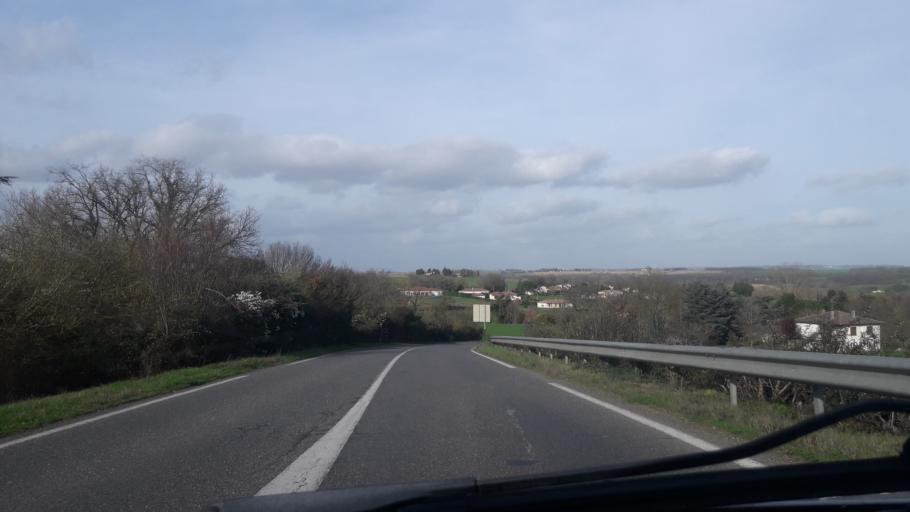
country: FR
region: Midi-Pyrenees
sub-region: Departement du Gers
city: Gimont
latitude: 43.7280
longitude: 0.8861
